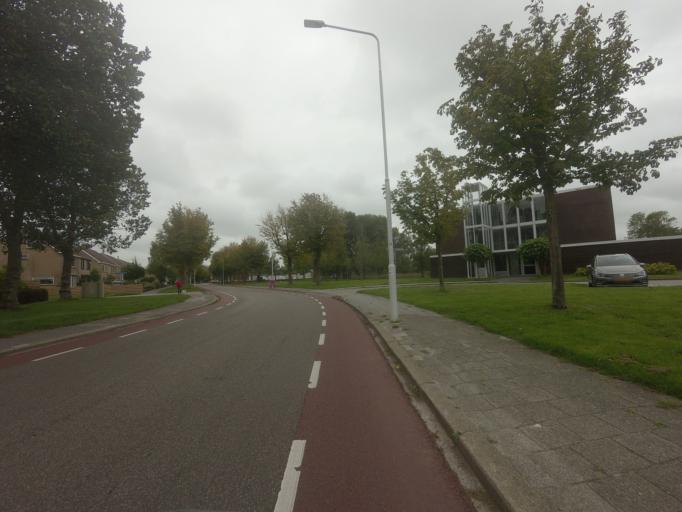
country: NL
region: Friesland
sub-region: Gemeente Leeuwarderadeel
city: Stiens
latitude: 53.2578
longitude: 5.7627
